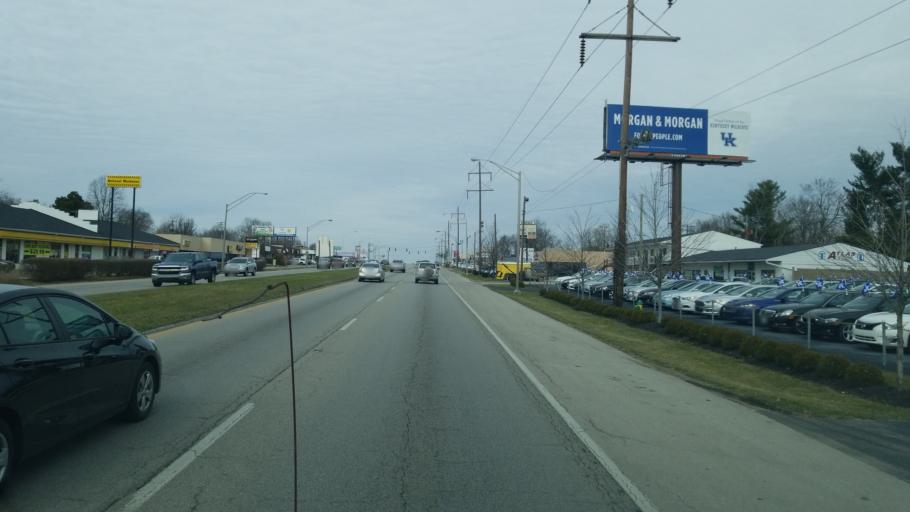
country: US
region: Kentucky
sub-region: Fayette County
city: Lexington-Fayette
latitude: 38.0536
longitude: -84.4586
